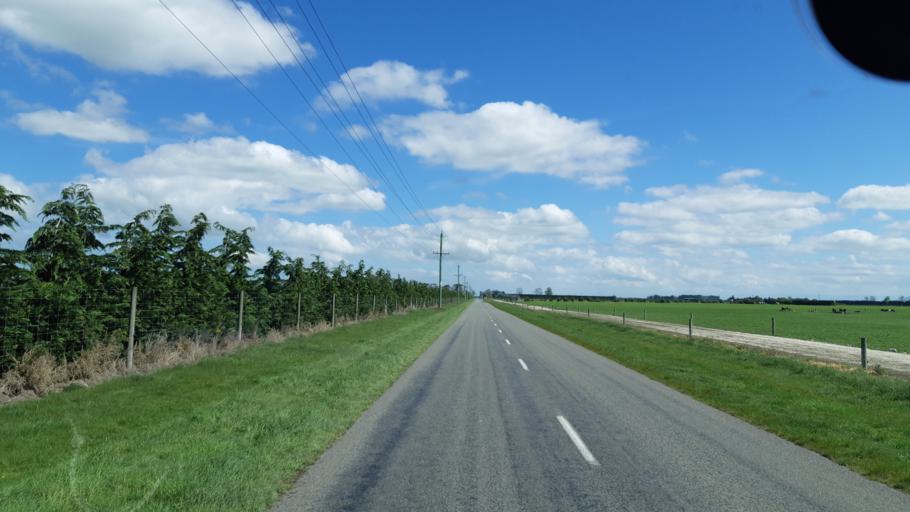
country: NZ
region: Canterbury
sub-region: Ashburton District
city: Tinwald
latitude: -43.9735
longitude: 171.4487
